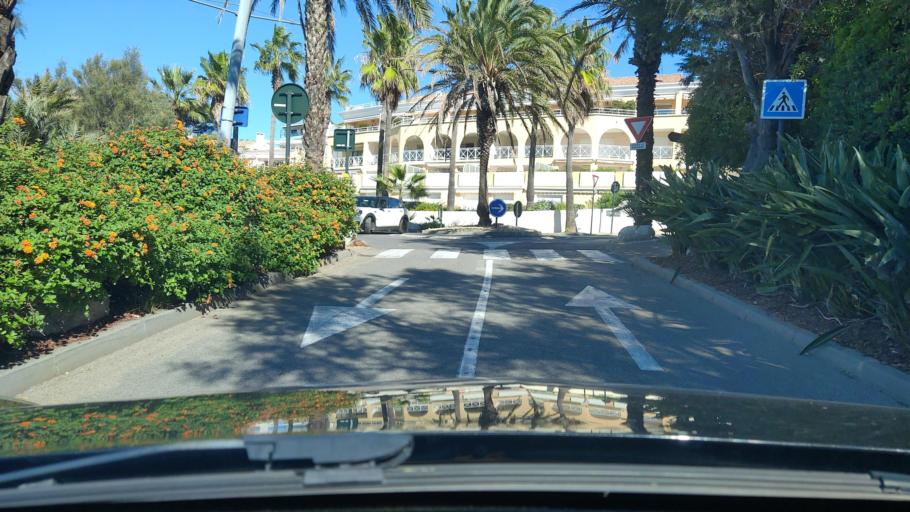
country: FR
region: Provence-Alpes-Cote d'Azur
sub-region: Departement du Var
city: Sanary-sur-Mer
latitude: 43.1160
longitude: 5.7903
